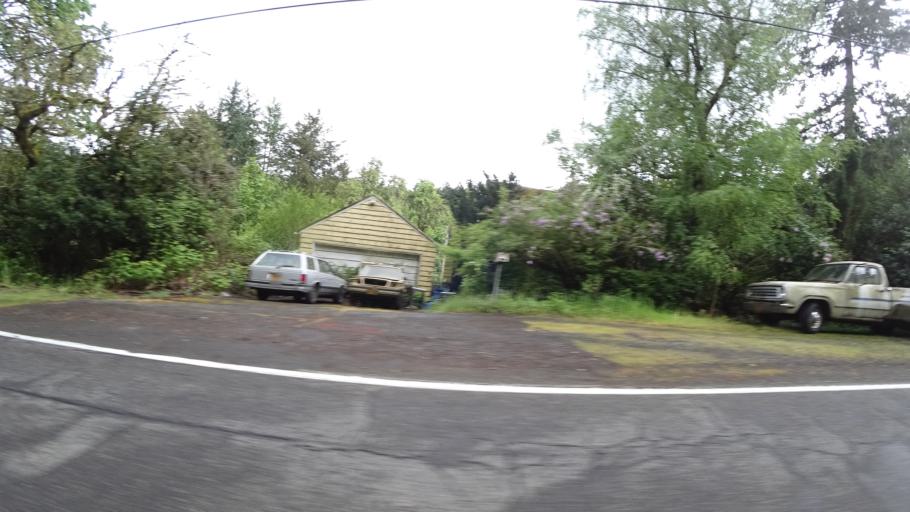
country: US
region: Oregon
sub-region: Washington County
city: West Haven
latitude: 45.5419
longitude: -122.7480
